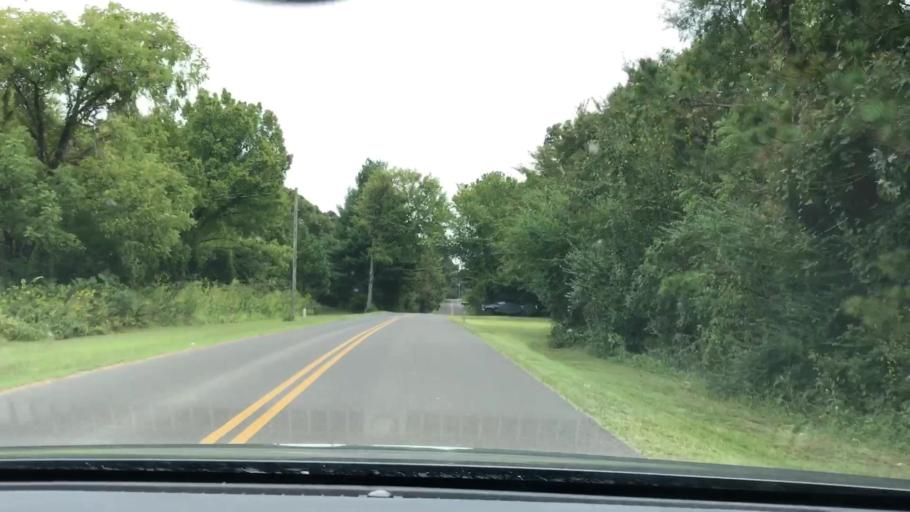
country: US
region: Kentucky
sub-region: Marshall County
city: Benton
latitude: 36.8318
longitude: -88.3677
